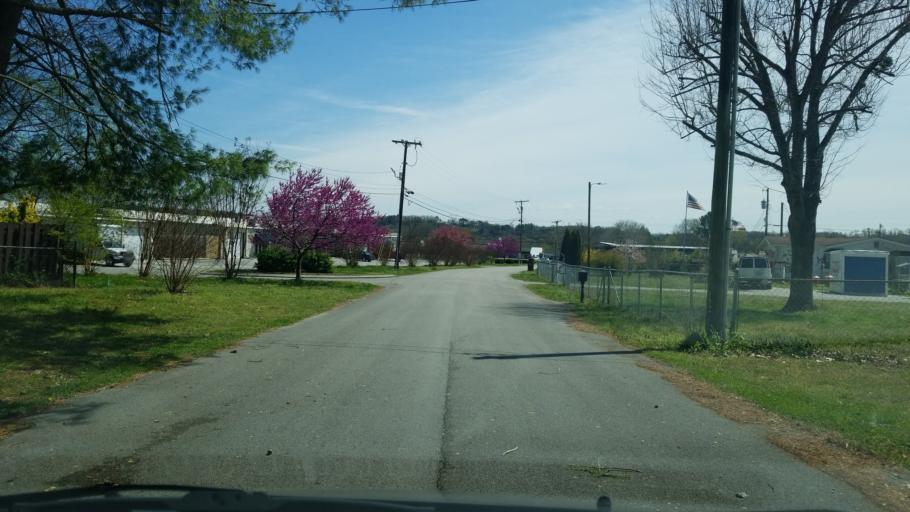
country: US
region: Tennessee
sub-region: Hamilton County
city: Soddy-Daisy
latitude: 35.2266
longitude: -85.2178
